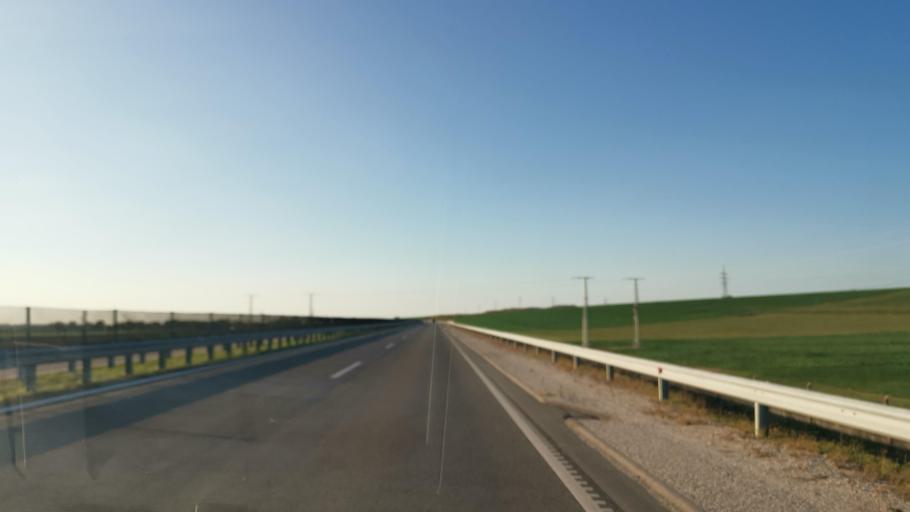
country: HU
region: Heves
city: Maklar
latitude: 47.8238
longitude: 20.3968
